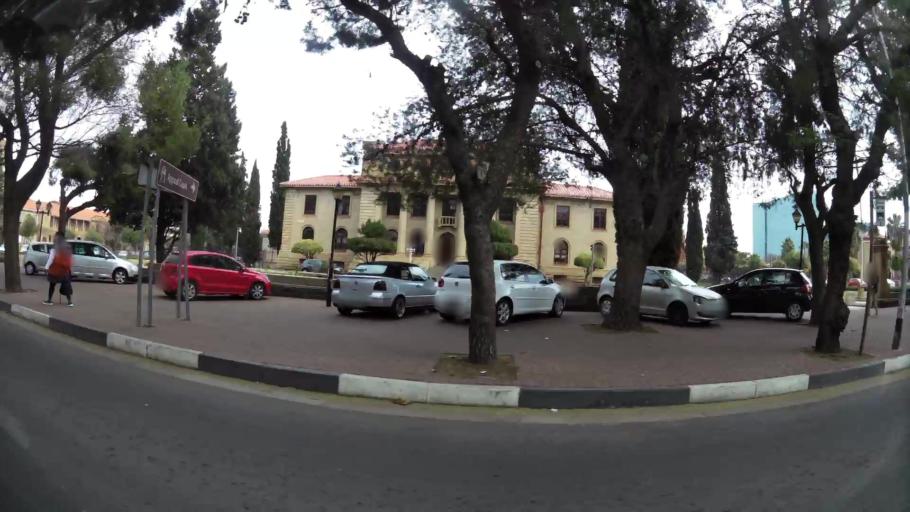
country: ZA
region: Orange Free State
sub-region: Mangaung Metropolitan Municipality
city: Bloemfontein
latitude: -29.1155
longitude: 26.2170
